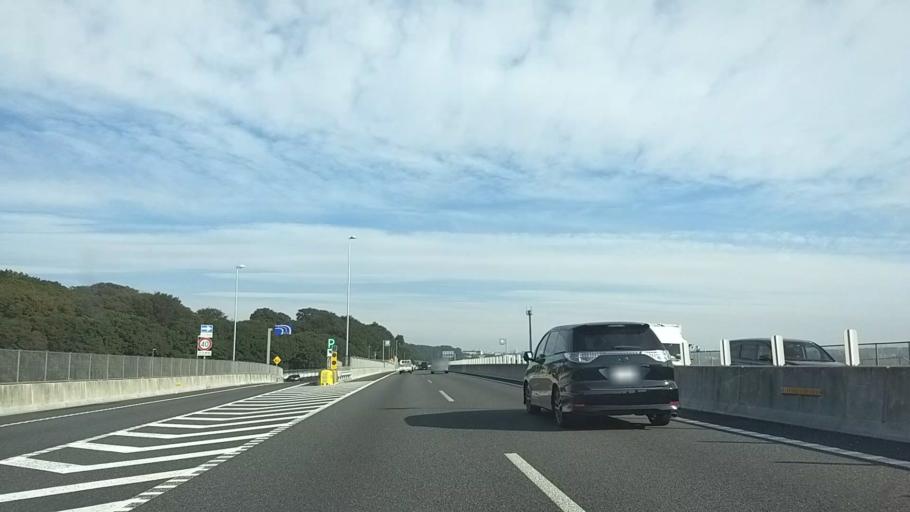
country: JP
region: Kanagawa
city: Zama
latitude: 35.4879
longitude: 139.3699
